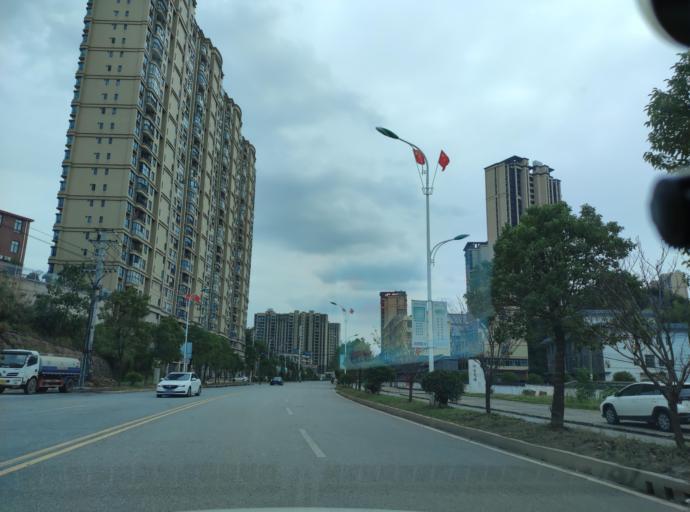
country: CN
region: Jiangxi Sheng
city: Pingxiang
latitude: 27.6799
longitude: 113.9090
